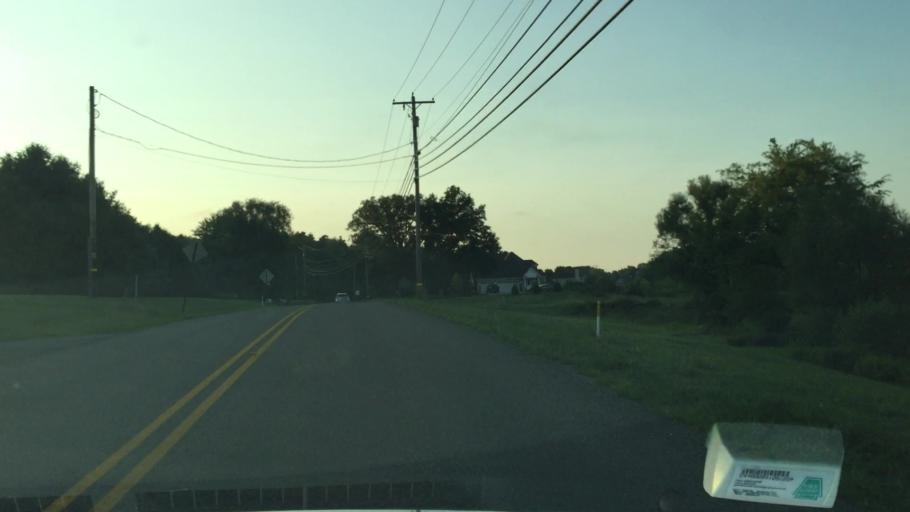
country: US
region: Pennsylvania
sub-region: Butler County
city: Seven Fields
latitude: 40.7015
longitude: -80.0497
